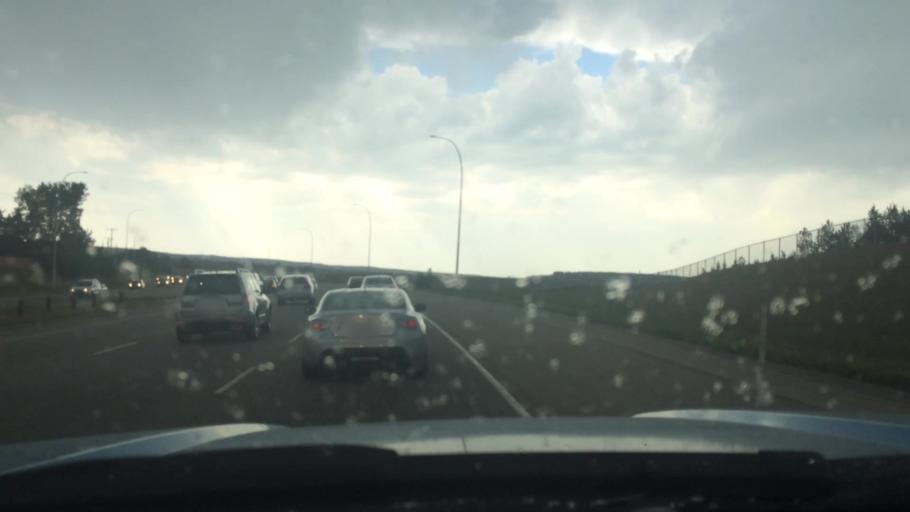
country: CA
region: Alberta
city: Calgary
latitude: 51.1300
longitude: -114.0567
